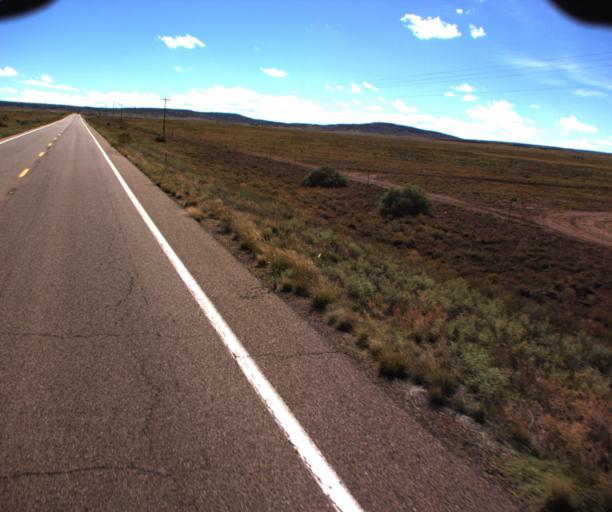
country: US
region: Arizona
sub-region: Apache County
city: Saint Johns
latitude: 34.5100
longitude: -109.6210
